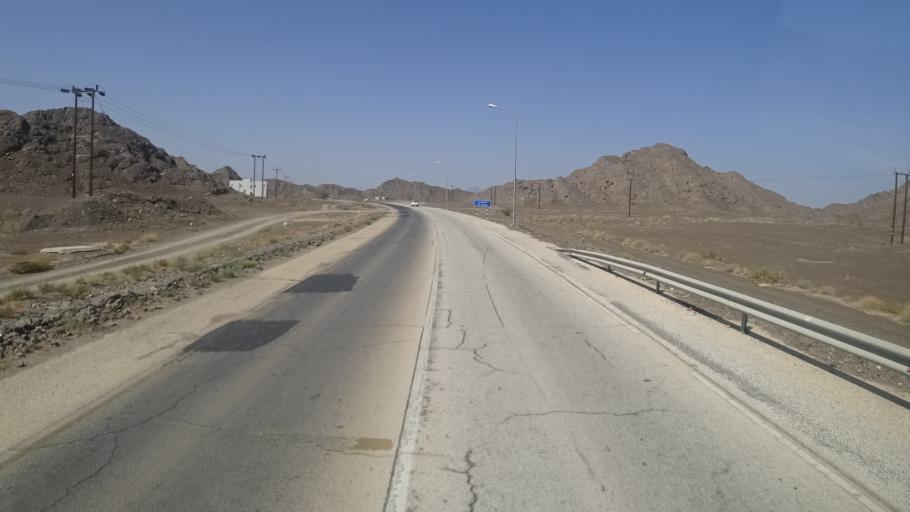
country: OM
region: Ash Sharqiyah
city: Ibra'
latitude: 22.6864
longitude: 58.5769
